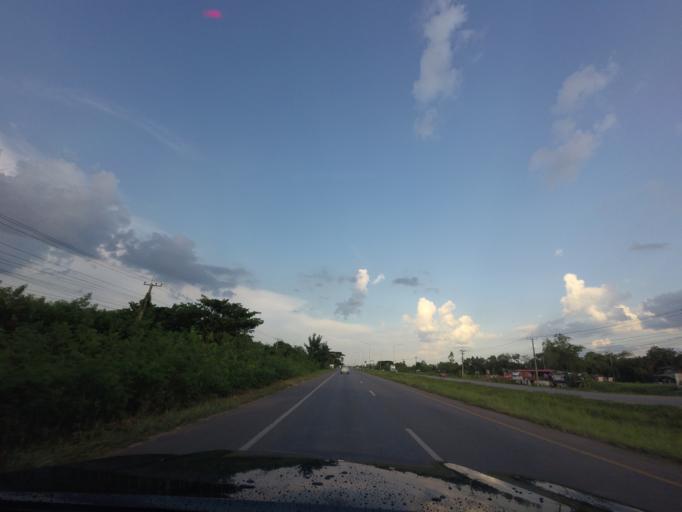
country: TH
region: Khon Kaen
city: Khon Kaen
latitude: 16.3979
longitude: 102.8630
